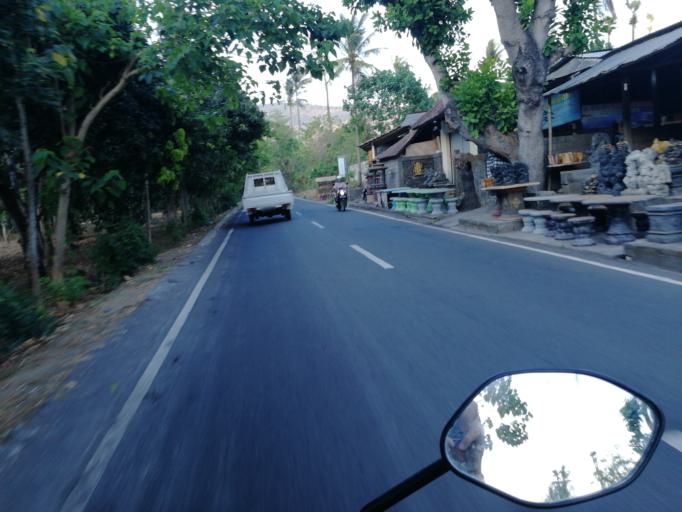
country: ID
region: Bali
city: Banjar Buayang
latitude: -8.3406
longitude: 115.6194
